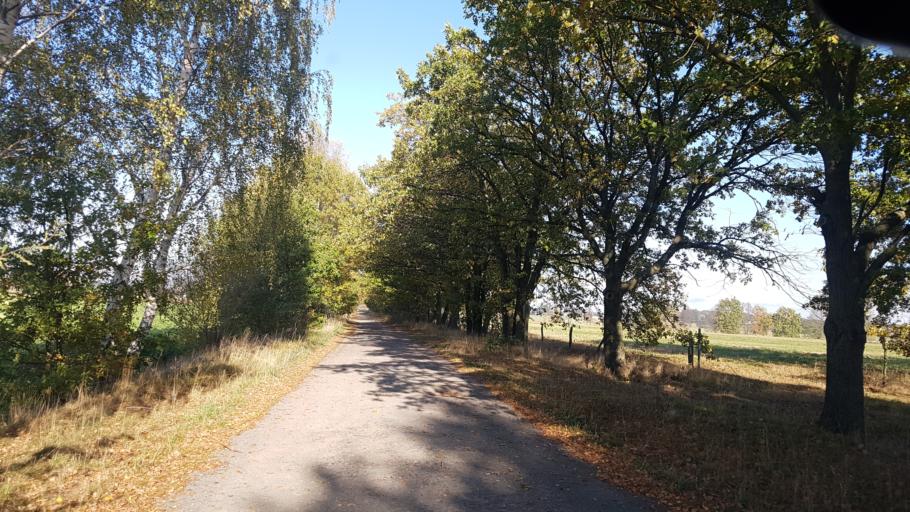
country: DE
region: Brandenburg
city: Ruckersdorf
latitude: 51.5555
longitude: 13.5405
